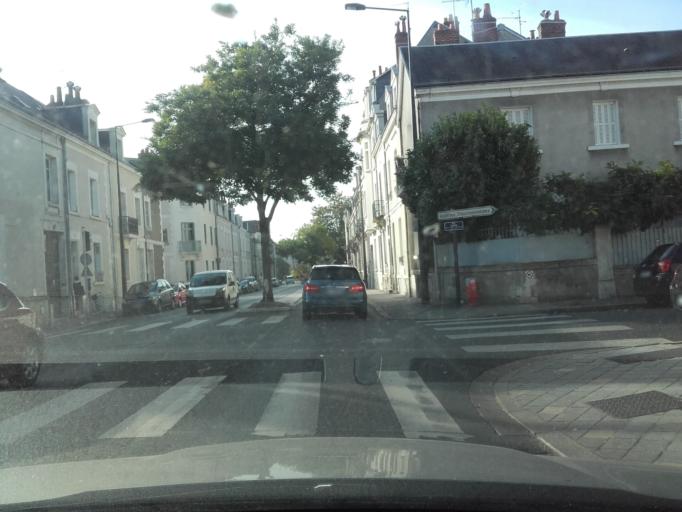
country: FR
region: Centre
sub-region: Departement d'Indre-et-Loire
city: Tours
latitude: 47.3953
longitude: 0.6998
